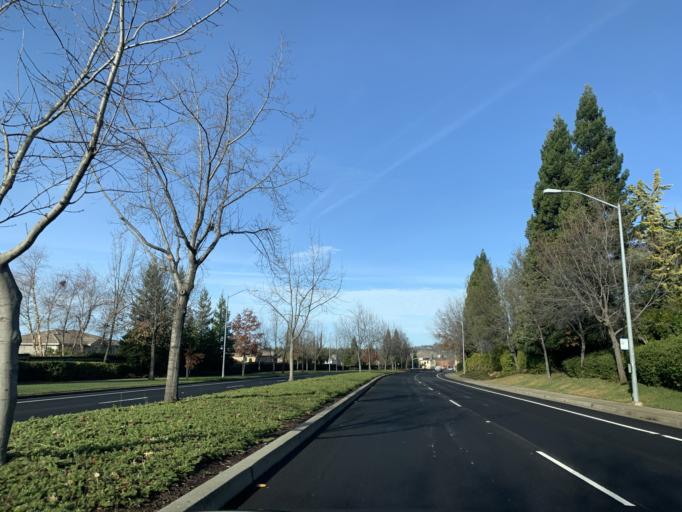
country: US
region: California
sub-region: El Dorado County
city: El Dorado Hills
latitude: 38.6755
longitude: -121.1067
